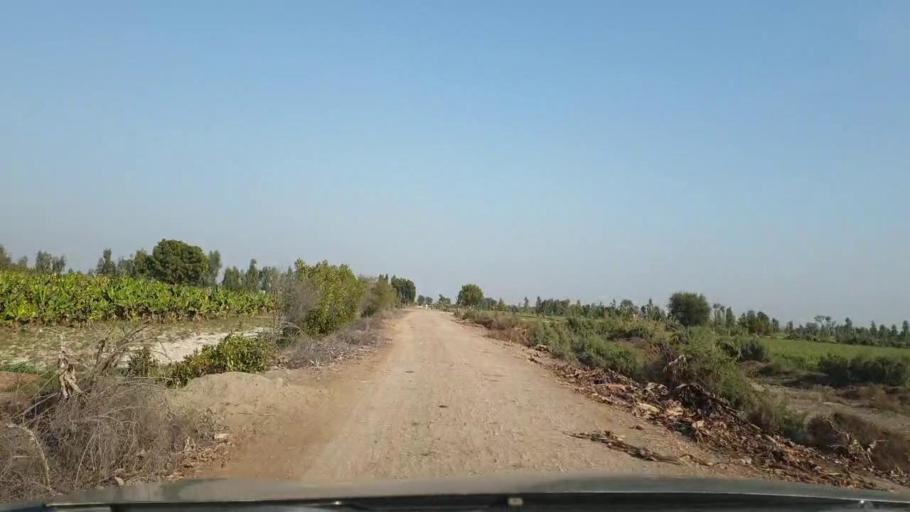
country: PK
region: Sindh
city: Berani
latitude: 25.6849
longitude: 68.8194
